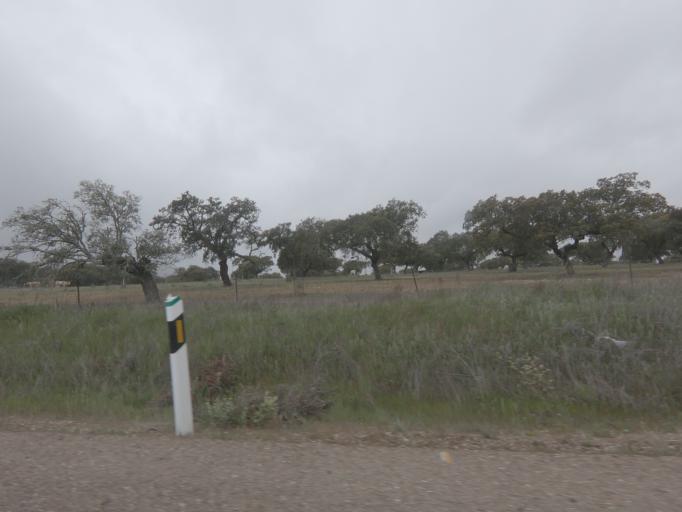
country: ES
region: Extremadura
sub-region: Provincia de Badajoz
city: Puebla de Obando
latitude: 39.2064
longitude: -6.5862
